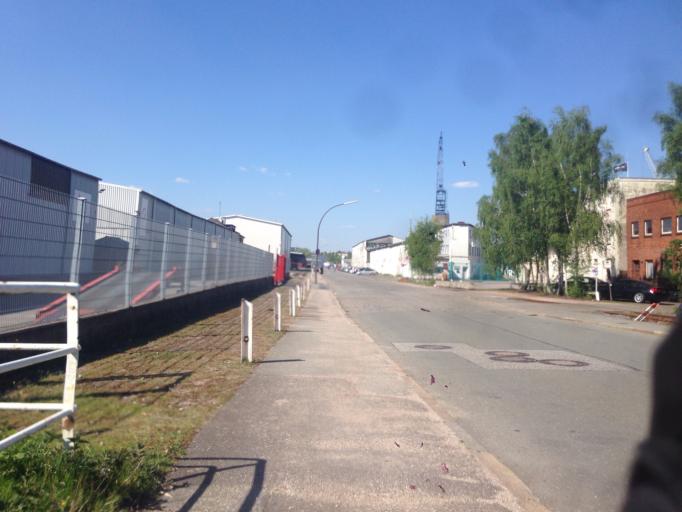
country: DE
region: Hamburg
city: Kleiner Grasbrook
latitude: 53.5334
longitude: 9.9728
